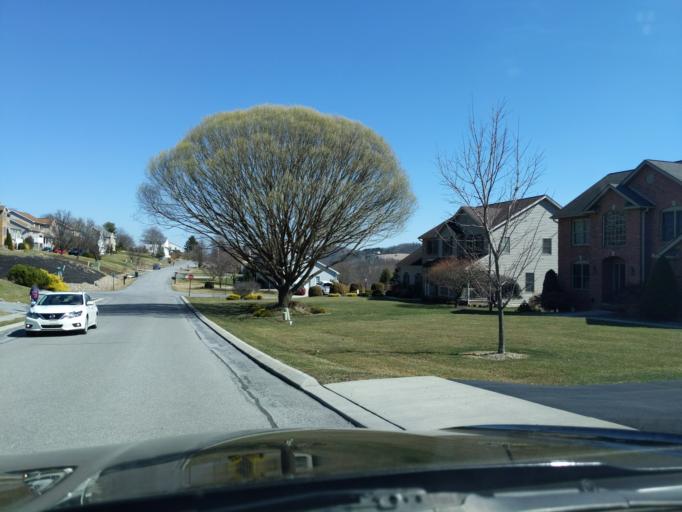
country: US
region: Pennsylvania
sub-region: Blair County
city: Duncansville
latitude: 40.4134
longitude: -78.4206
